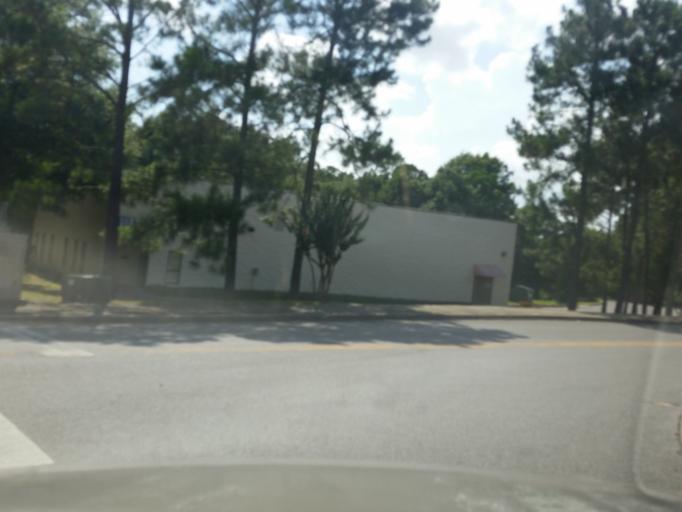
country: US
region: Florida
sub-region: Escambia County
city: Brent
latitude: 30.4801
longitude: -87.2668
